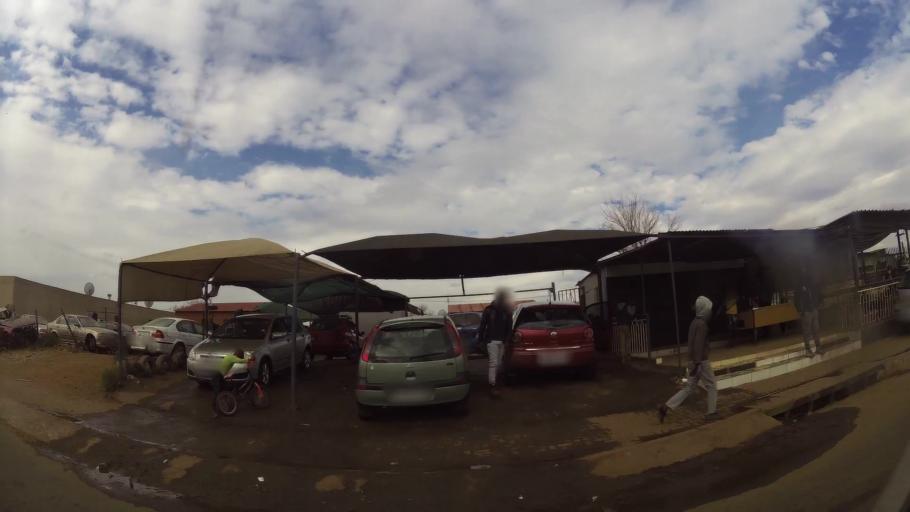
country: ZA
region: Gauteng
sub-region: Ekurhuleni Metropolitan Municipality
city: Germiston
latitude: -26.4052
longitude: 28.1542
